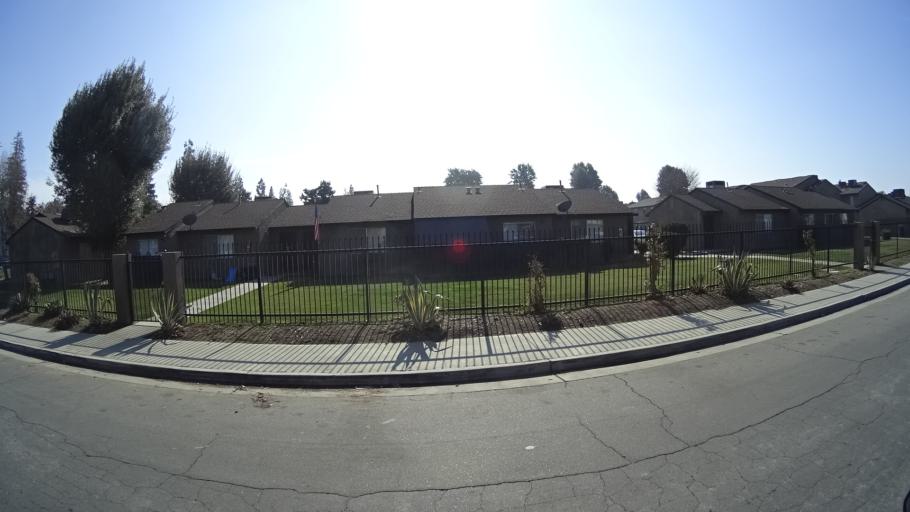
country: US
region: California
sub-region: Kern County
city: Bakersfield
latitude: 35.3962
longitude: -119.0109
